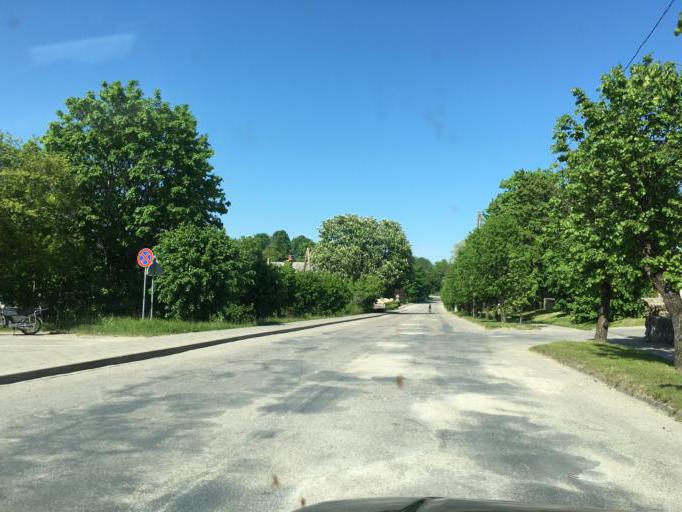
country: LV
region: Dundaga
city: Dundaga
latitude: 57.5101
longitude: 22.3511
